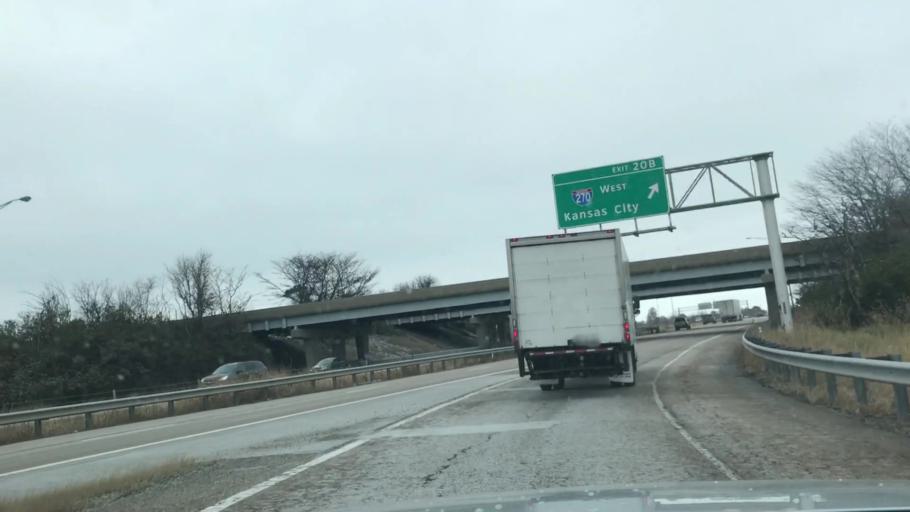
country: US
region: Illinois
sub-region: Madison County
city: Troy
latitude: 38.7514
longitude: -89.9071
